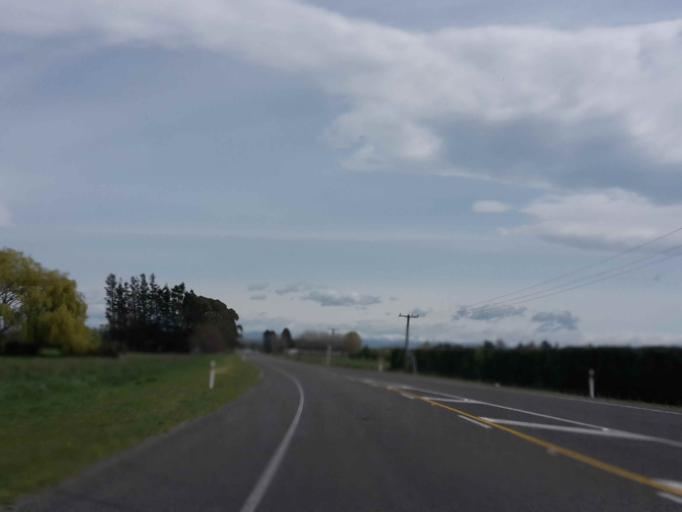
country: NZ
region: Canterbury
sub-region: Waimakariri District
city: Kaiapoi
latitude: -43.3972
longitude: 172.6046
